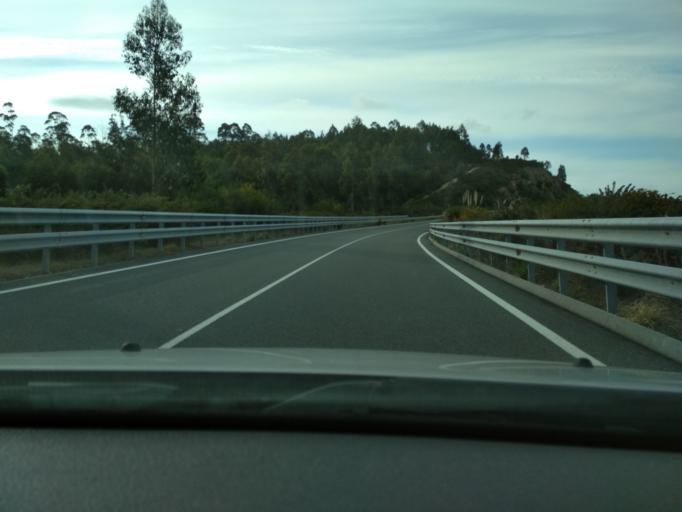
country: ES
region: Galicia
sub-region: Provincia da Coruna
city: Culleredo
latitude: 43.2879
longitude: -8.4013
